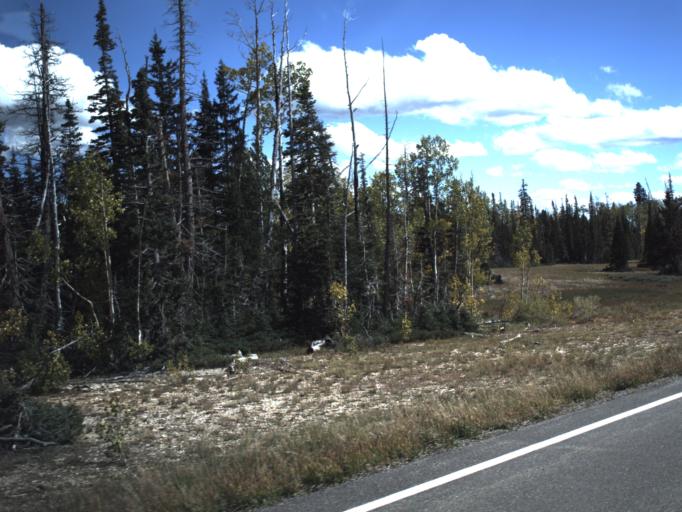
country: US
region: Utah
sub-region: Iron County
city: Parowan
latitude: 37.5511
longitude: -112.7870
